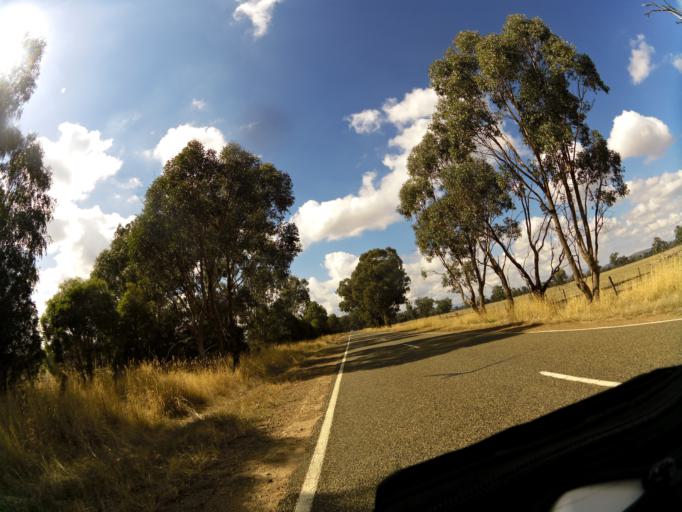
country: AU
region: Victoria
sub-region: Benalla
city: Benalla
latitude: -36.6096
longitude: 146.0188
